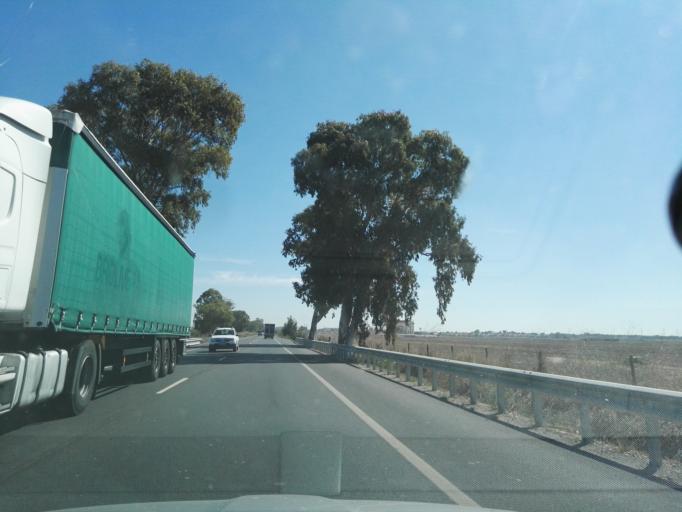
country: PT
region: Santarem
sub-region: Benavente
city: Samora Correia
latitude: 38.9302
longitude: -8.9084
